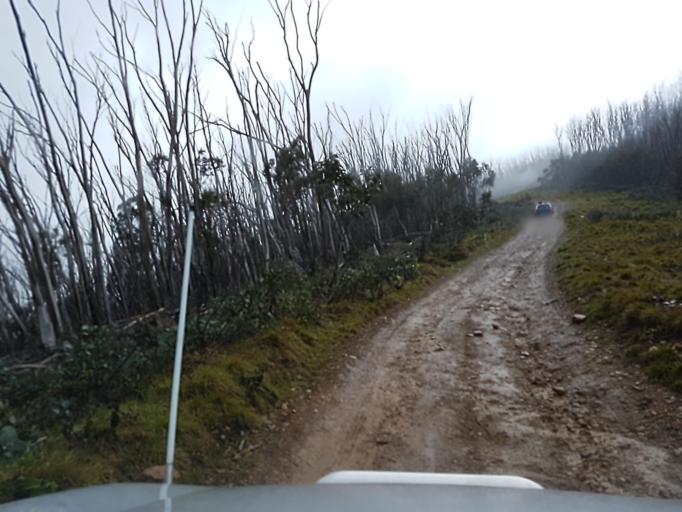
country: AU
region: Victoria
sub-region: Alpine
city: Mount Beauty
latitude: -37.0900
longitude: 147.0991
